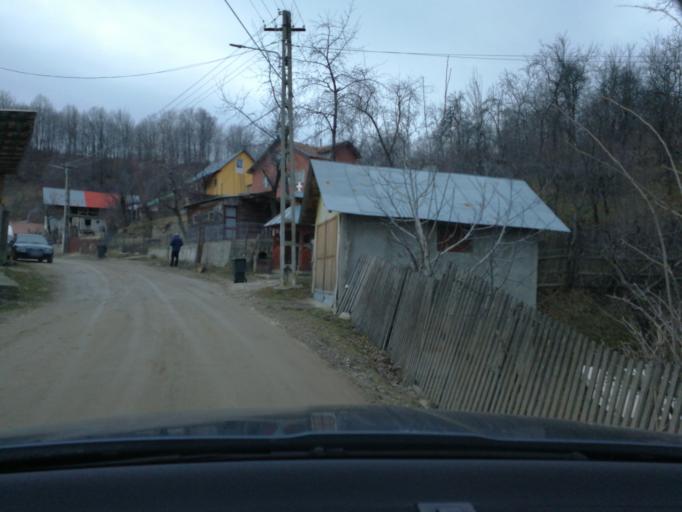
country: RO
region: Dambovita
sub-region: Comuna Bezdead
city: Bezdead
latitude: 45.1726
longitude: 25.5541
